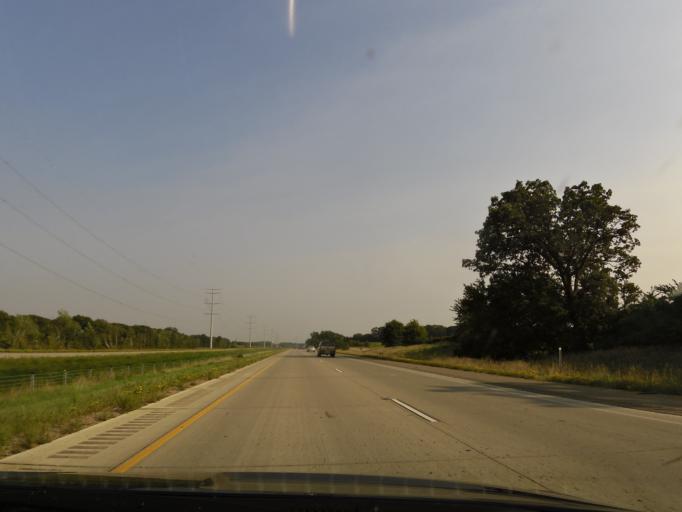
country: US
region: Minnesota
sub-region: Wright County
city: Clearwater
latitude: 45.4346
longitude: -94.1048
